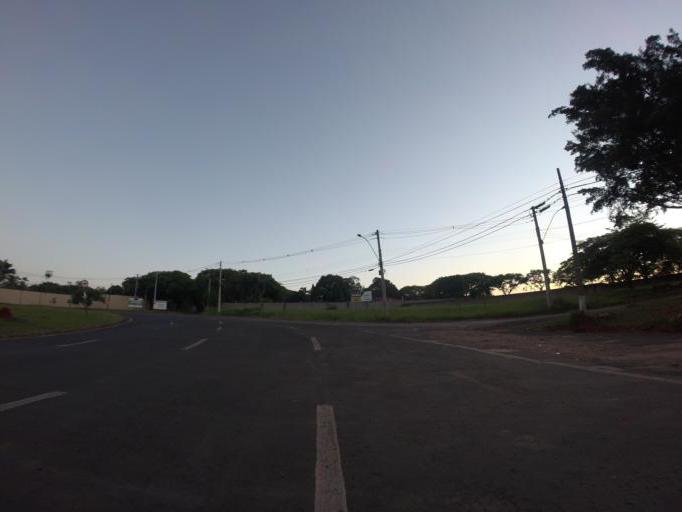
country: BR
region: Sao Paulo
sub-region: Piracicaba
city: Piracicaba
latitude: -22.7525
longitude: -47.5950
